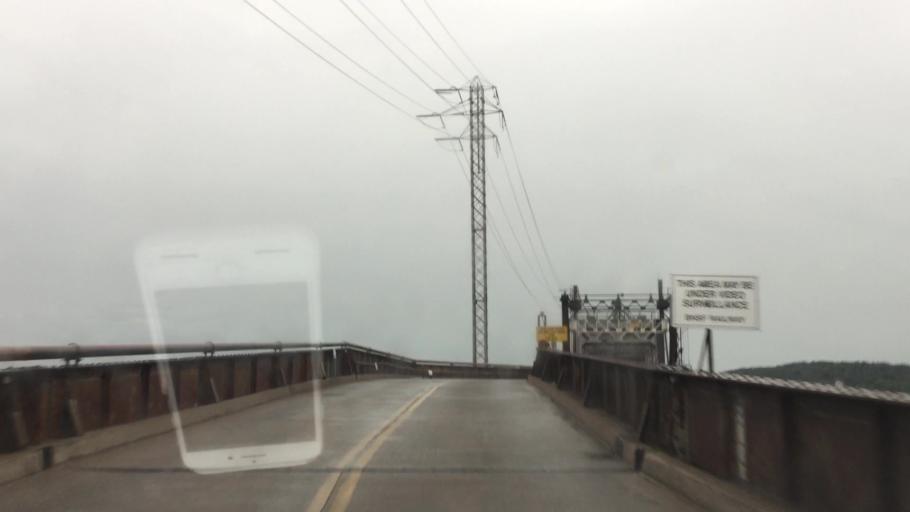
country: US
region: Iowa
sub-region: Lee County
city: Fort Madison
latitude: 40.6292
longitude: -91.2983
